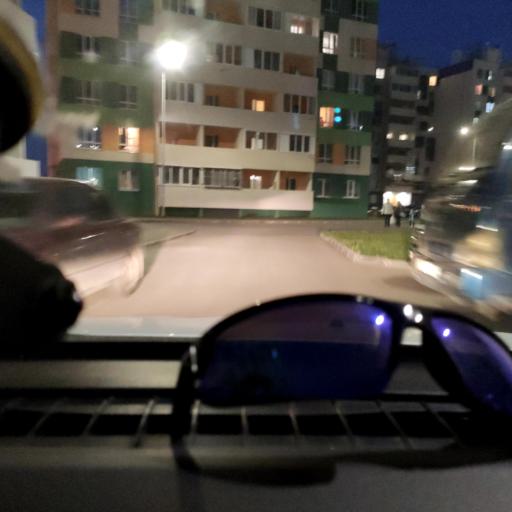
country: RU
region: Samara
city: Samara
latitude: 53.0969
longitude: 50.1625
